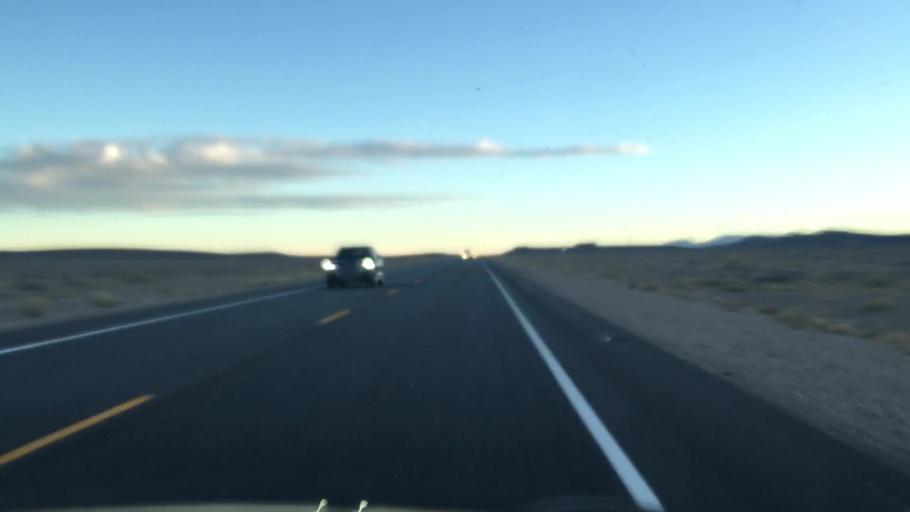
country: US
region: Nevada
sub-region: Esmeralda County
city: Goldfield
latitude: 37.4198
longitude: -117.1564
